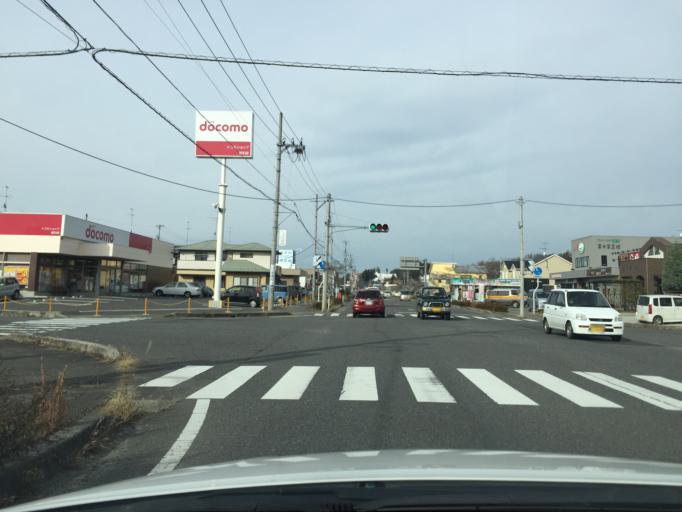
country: JP
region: Fukushima
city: Funehikimachi-funehiki
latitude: 37.4415
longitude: 140.5876
